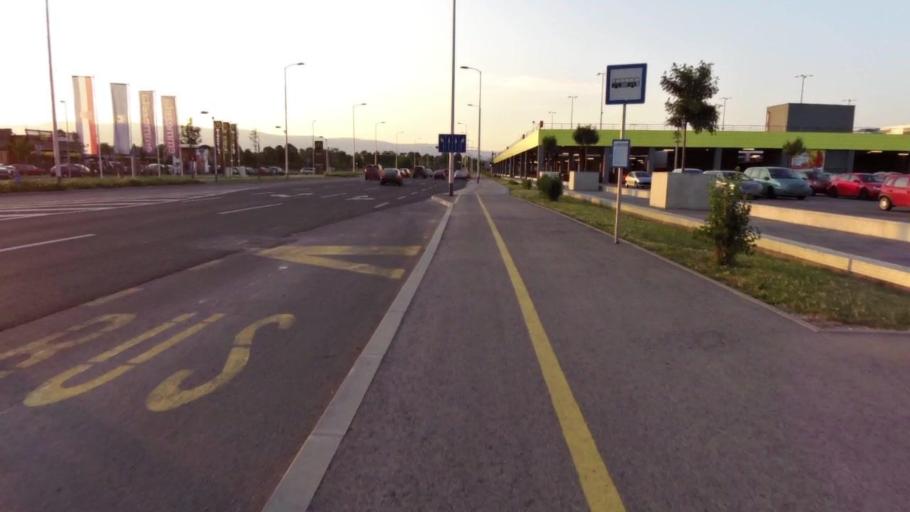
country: HR
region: Grad Zagreb
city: Dubrava
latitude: 45.8012
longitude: 16.0489
